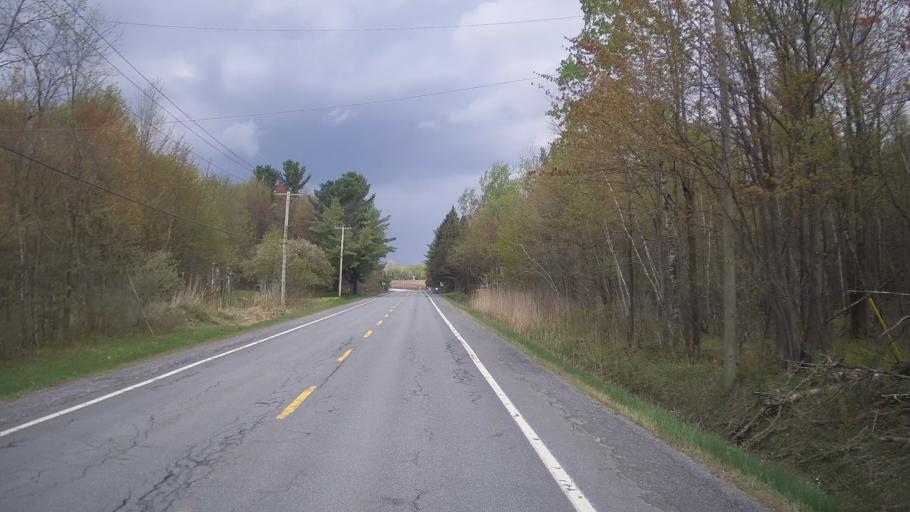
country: CA
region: Quebec
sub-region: Monteregie
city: Farnham
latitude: 45.2388
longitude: -72.8813
